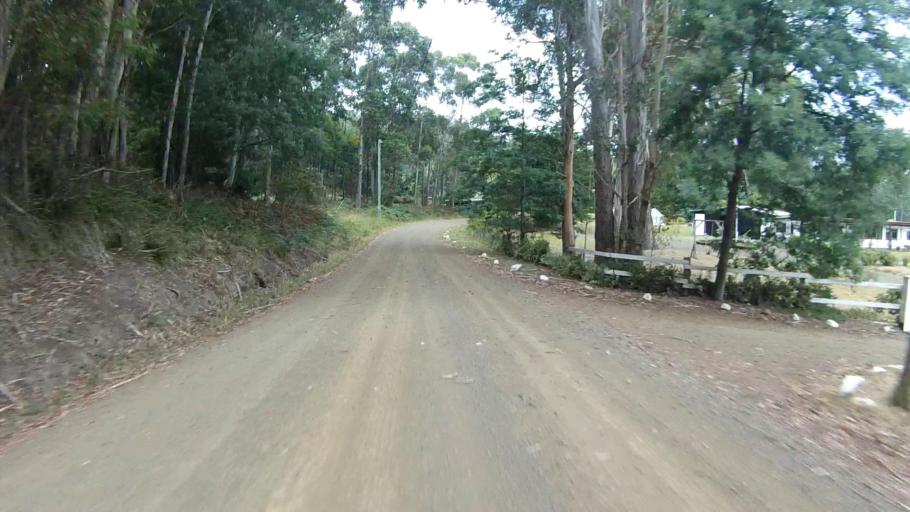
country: AU
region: Tasmania
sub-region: Huon Valley
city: Cygnet
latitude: -43.2318
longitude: 147.1590
